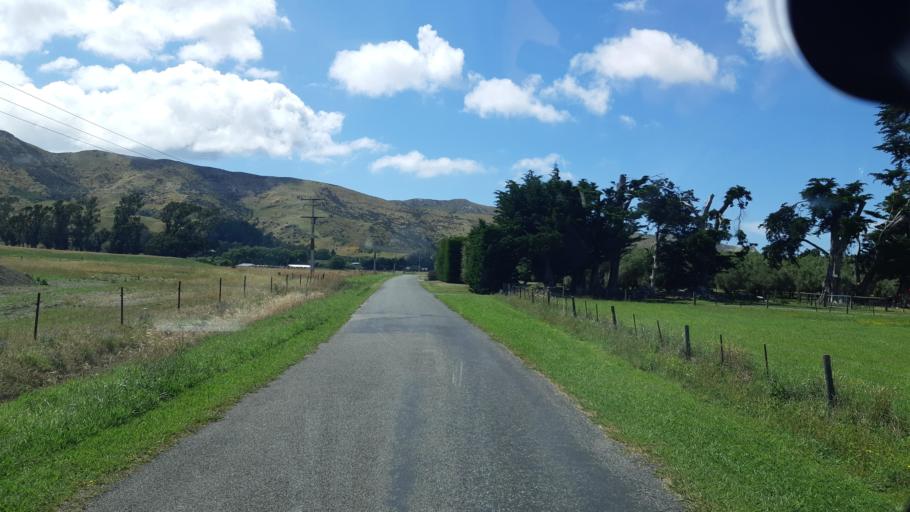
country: NZ
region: Marlborough
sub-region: Marlborough District
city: Blenheim
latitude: -41.8061
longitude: 174.1487
